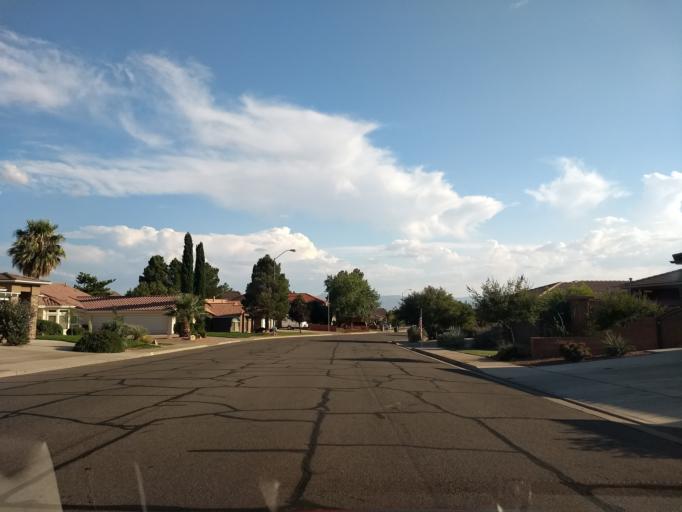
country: US
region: Utah
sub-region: Washington County
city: Saint George
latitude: 37.1100
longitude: -113.5511
